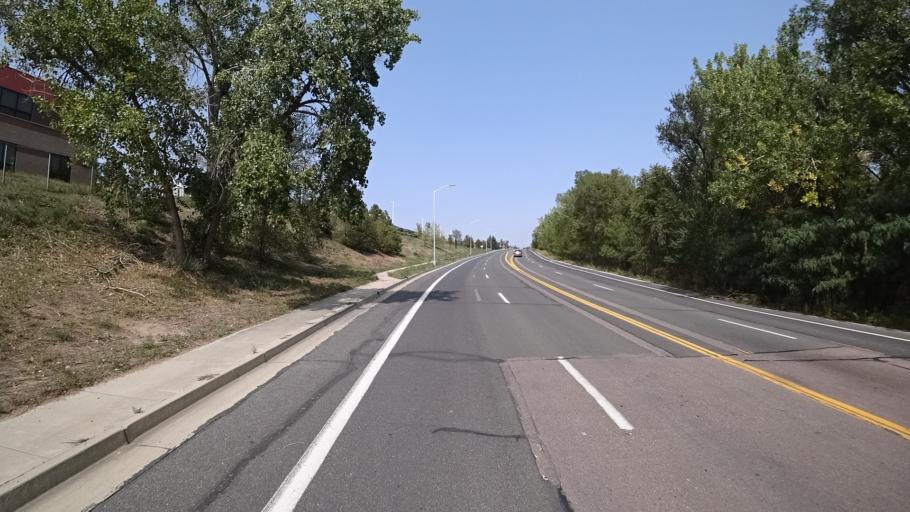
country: US
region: Colorado
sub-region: El Paso County
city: Colorado Springs
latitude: 38.8163
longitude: -104.8046
